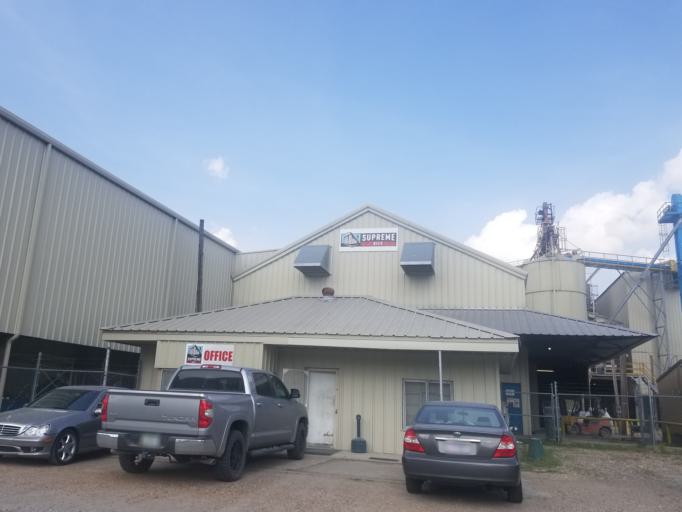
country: US
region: Arkansas
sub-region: Crittenden County
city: Marion
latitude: 35.2225
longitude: -90.3265
